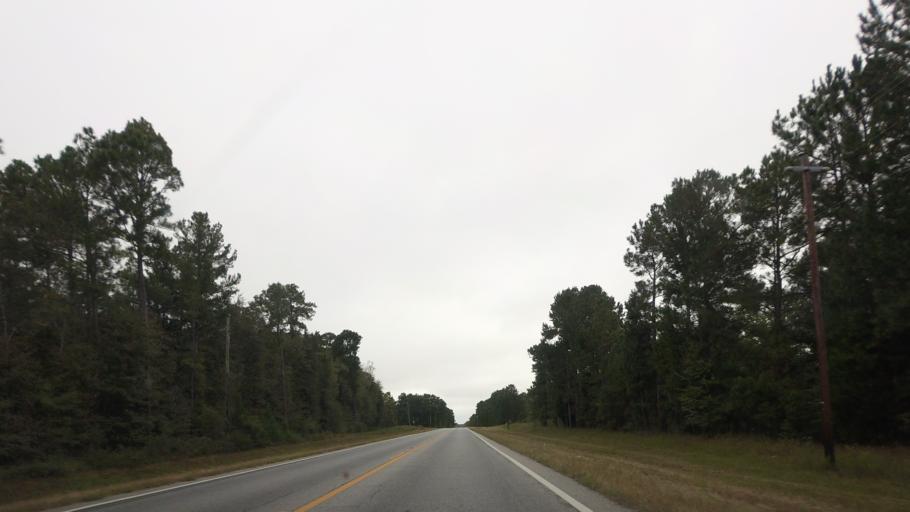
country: US
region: Georgia
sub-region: Berrien County
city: Nashville
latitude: 31.1559
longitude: -83.2238
